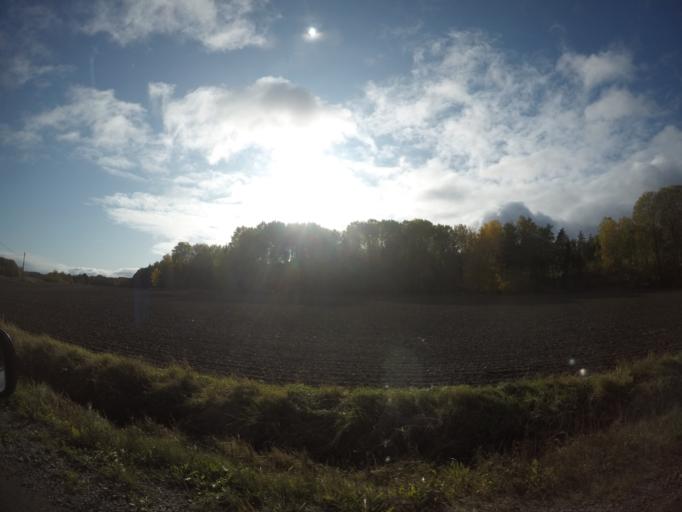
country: SE
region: Soedermanland
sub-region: Eskilstuna Kommun
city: Kvicksund
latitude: 59.3839
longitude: 16.2421
